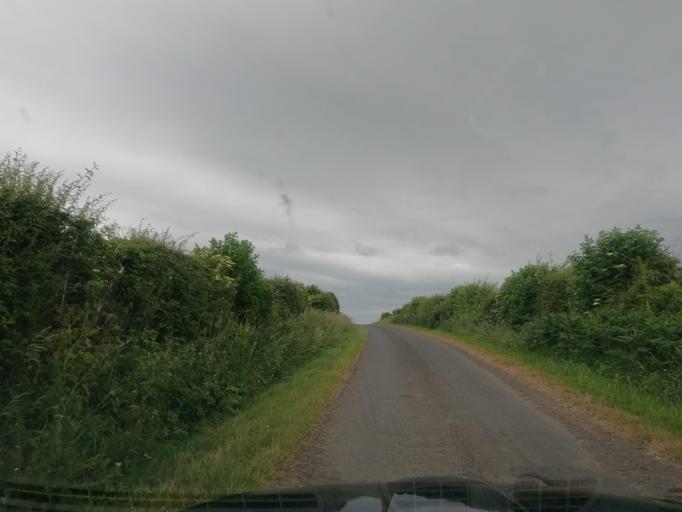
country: GB
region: England
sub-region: Northumberland
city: Ford
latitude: 55.6677
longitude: -2.0855
